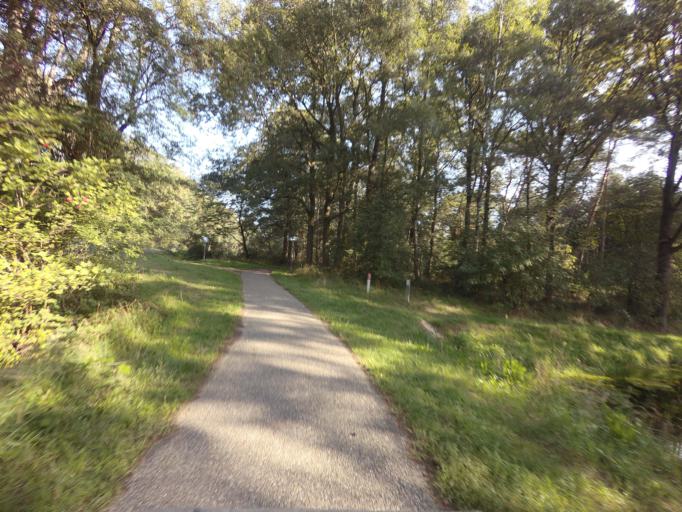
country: NL
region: Overijssel
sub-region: Gemeente Raalte
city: Raalte
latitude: 52.3431
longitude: 6.2719
